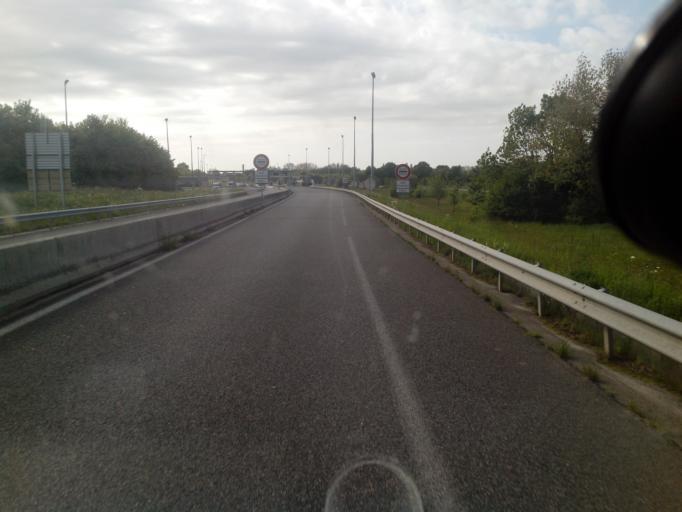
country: FR
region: Haute-Normandie
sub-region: Departement de l'Eure
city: Beuzeville
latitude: 49.3202
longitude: 0.3119
